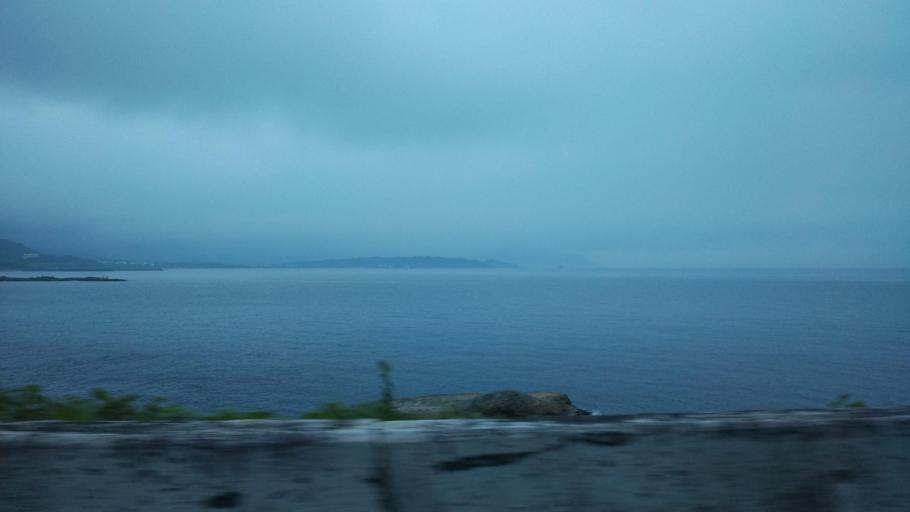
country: TW
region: Taiwan
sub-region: Keelung
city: Keelung
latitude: 25.2048
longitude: 121.6828
